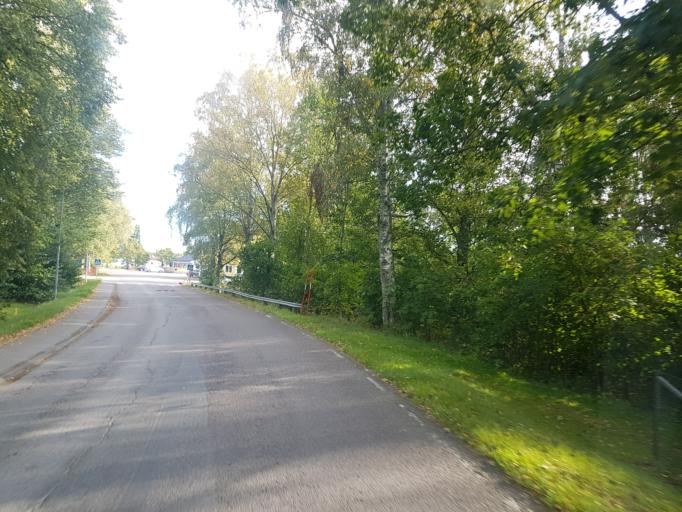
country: SE
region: Dalarna
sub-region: Borlange Kommun
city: Ornas
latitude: 60.4121
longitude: 15.6097
